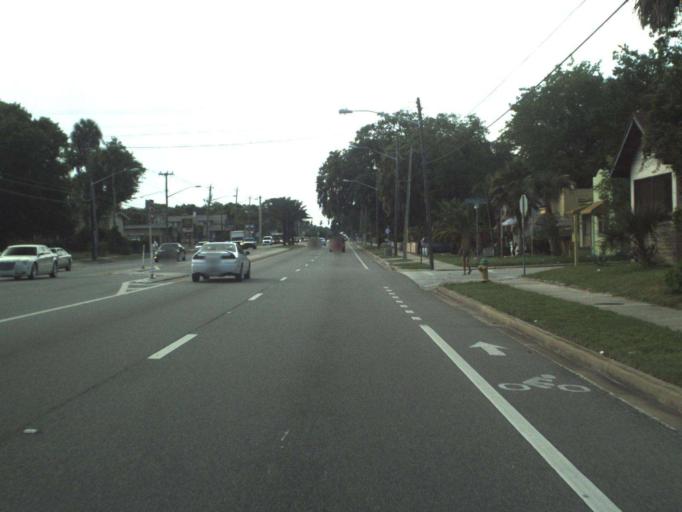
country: US
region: Florida
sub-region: Volusia County
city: Daytona Beach
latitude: 29.1952
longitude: -81.0143
